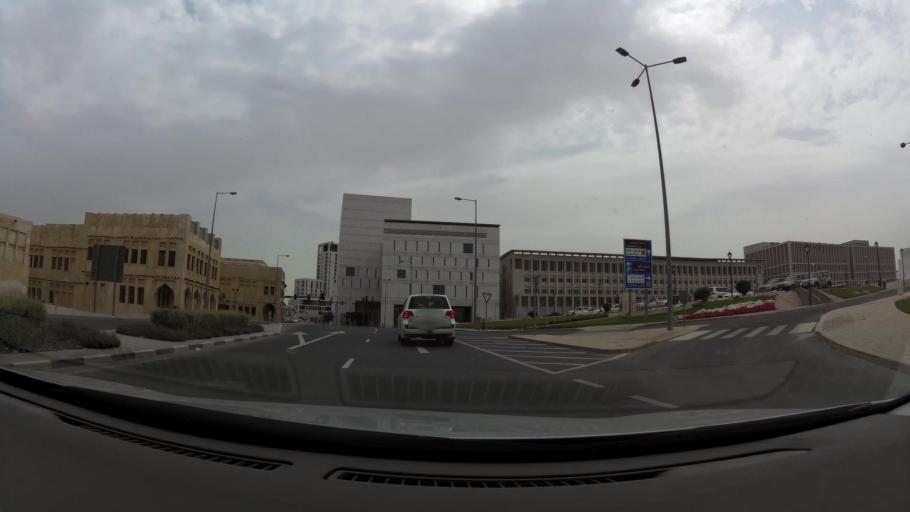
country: QA
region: Baladiyat ad Dawhah
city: Doha
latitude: 25.2892
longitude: 51.5298
